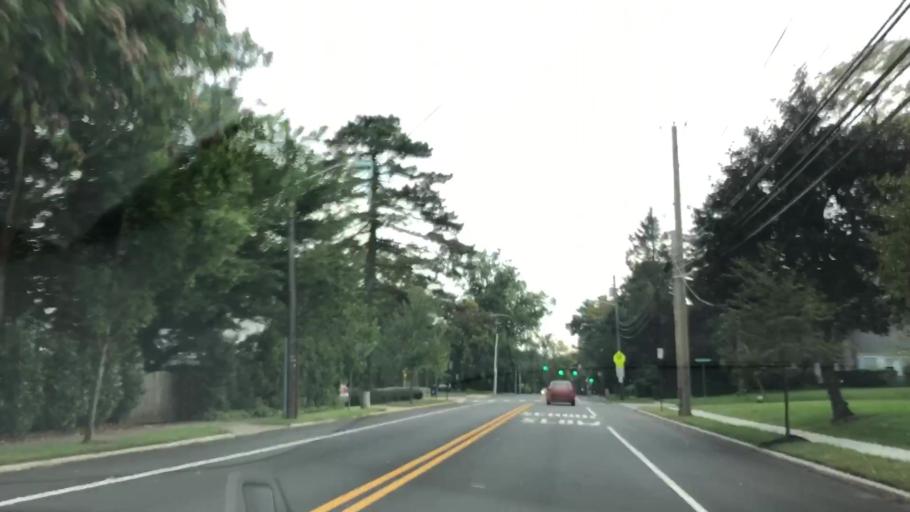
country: US
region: New Jersey
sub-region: Essex County
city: Upper Montclair
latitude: 40.8472
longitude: -74.1943
